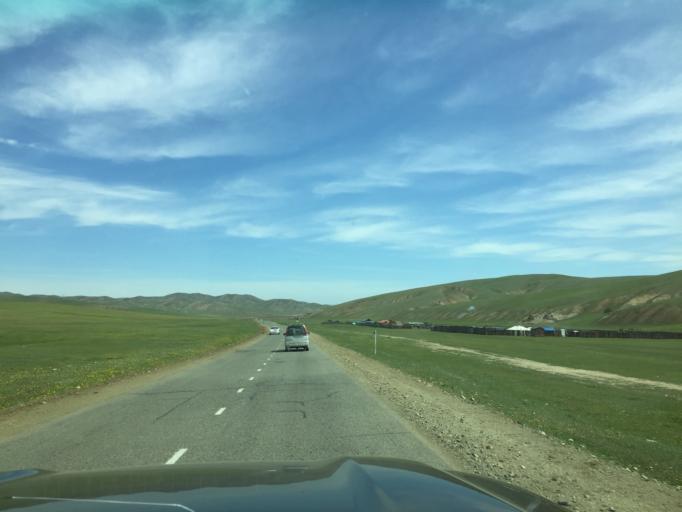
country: MN
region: Central Aimak
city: Bornuur
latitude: 48.6697
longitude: 106.1360
